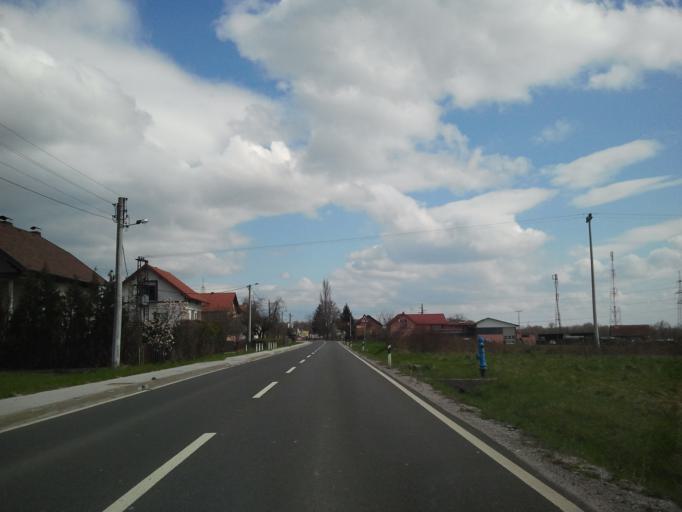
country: HR
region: Grad Zagreb
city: Horvati
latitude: 45.7107
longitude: 15.7759
